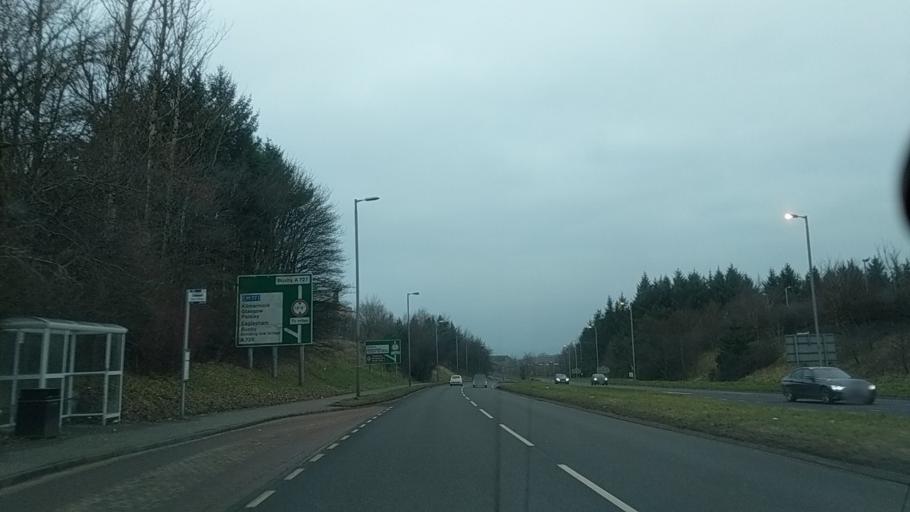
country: GB
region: Scotland
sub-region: Glasgow City
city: Carmunnock
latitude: 55.7673
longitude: -4.2189
